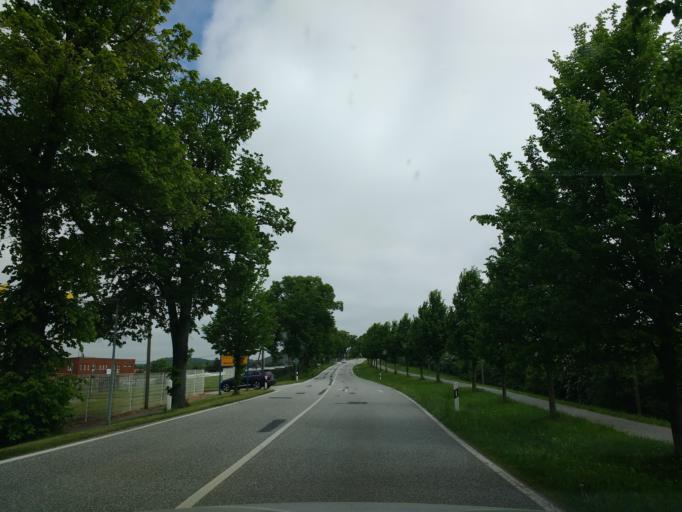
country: DE
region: Mecklenburg-Vorpommern
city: Neukloster
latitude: 53.8699
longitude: 11.6938
